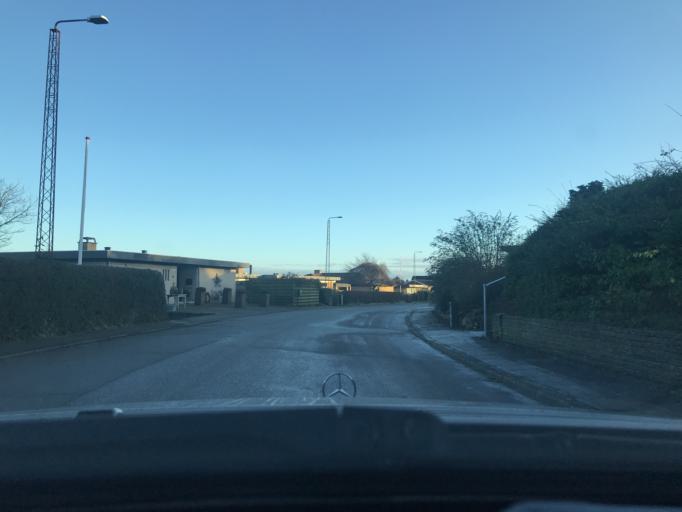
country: DK
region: South Denmark
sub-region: Sonderborg Kommune
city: Dybbol
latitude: 54.9163
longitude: 9.7641
